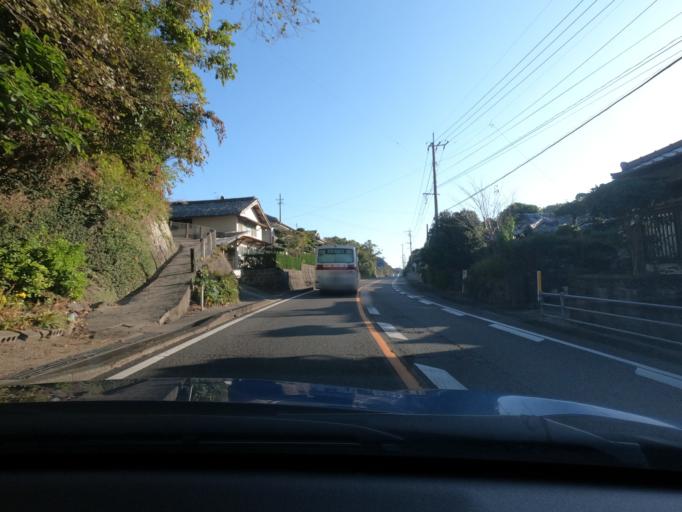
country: JP
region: Kagoshima
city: Akune
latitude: 31.9861
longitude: 130.2038
